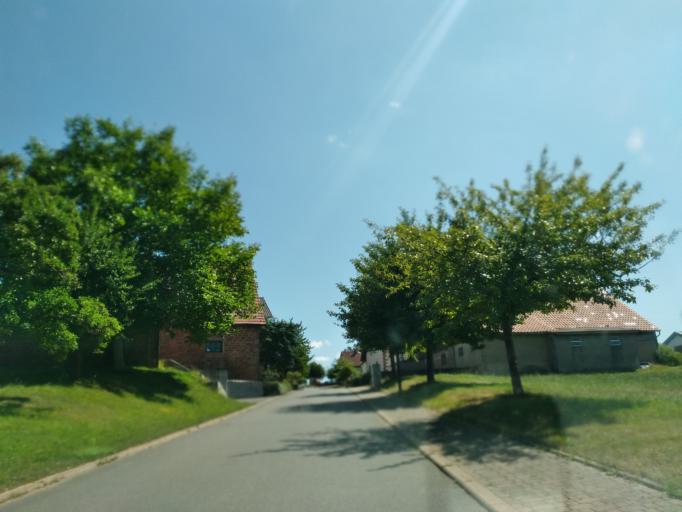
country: DE
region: Baden-Wuerttemberg
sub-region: Karlsruhe Region
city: Limbach
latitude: 49.4830
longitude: 9.2404
